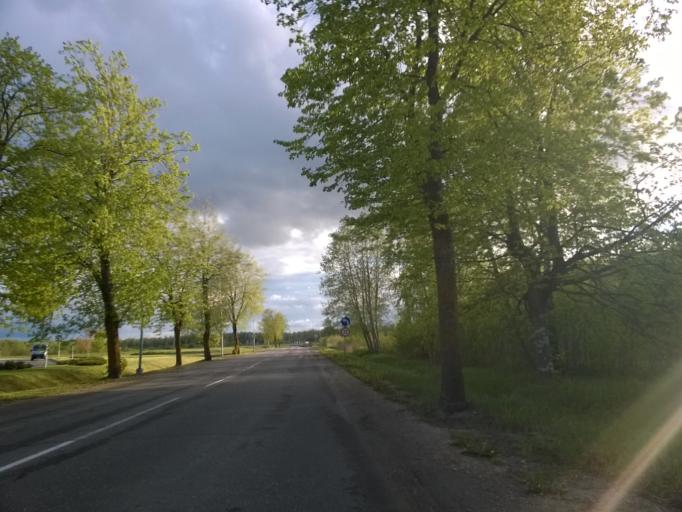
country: LV
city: Tireli
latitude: 56.9312
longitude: 23.5875
